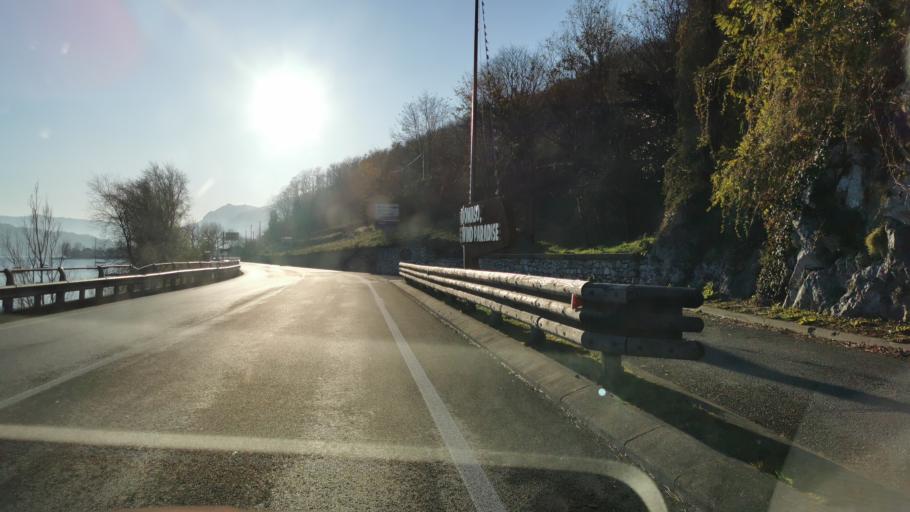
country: IT
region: Lombardy
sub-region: Provincia di Como
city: Vercana
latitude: 46.1623
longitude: 9.3451
